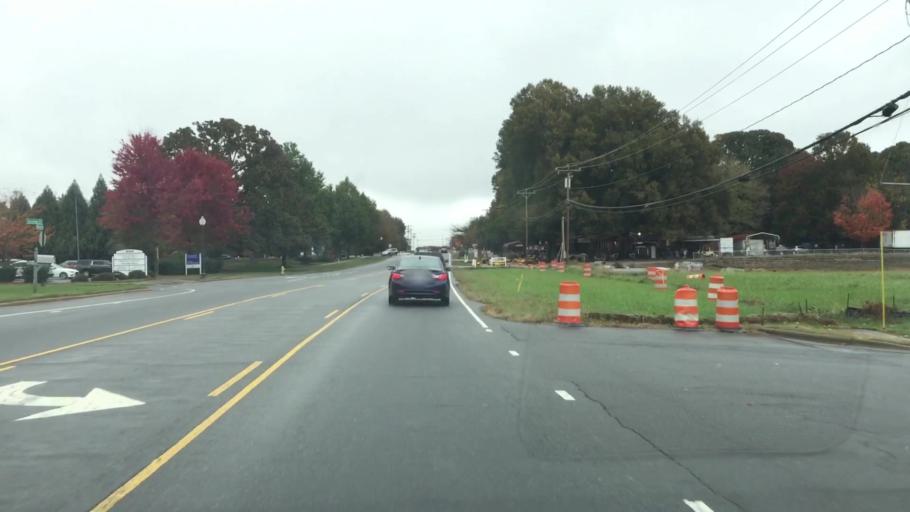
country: US
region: North Carolina
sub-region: Iredell County
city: Mooresville
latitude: 35.5899
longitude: -80.8737
